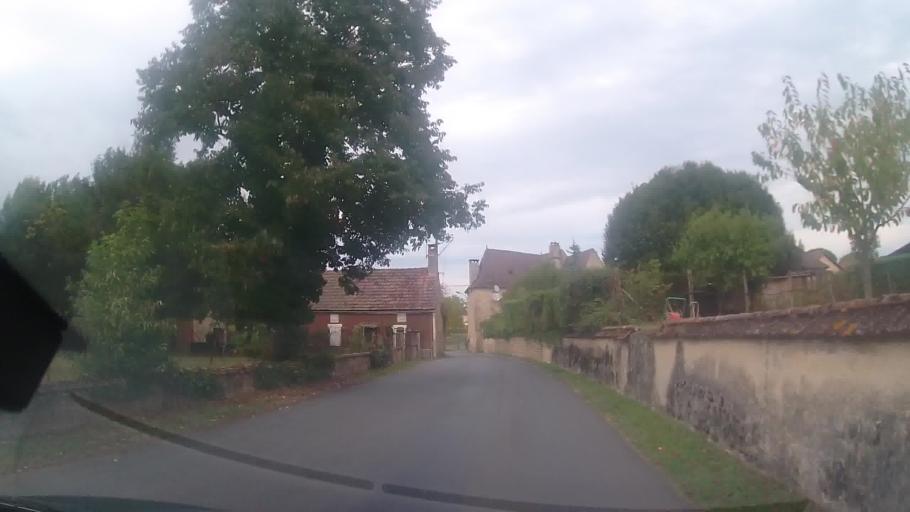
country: FR
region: Aquitaine
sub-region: Departement de la Dordogne
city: Eyvigues-et-Eybenes
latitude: 44.8582
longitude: 1.3665
